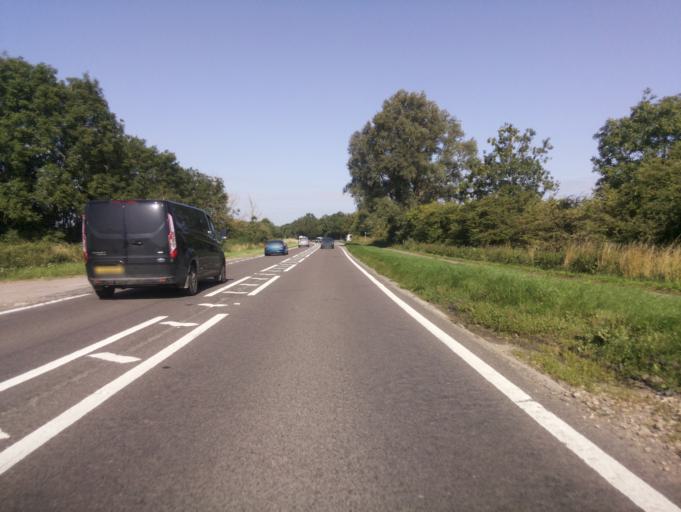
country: GB
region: England
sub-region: Oxfordshire
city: Eynsham
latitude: 51.7878
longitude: -1.3943
